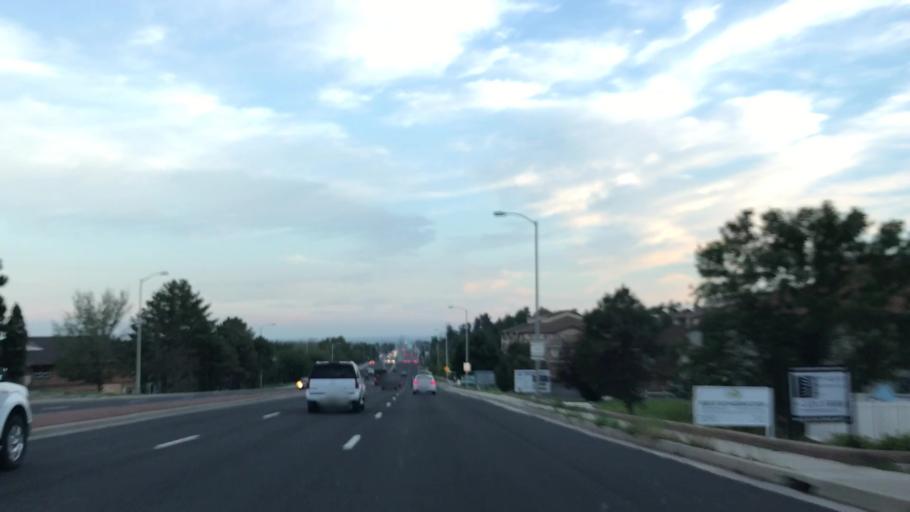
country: US
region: Colorado
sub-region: El Paso County
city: Cimarron Hills
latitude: 38.8753
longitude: -104.7572
